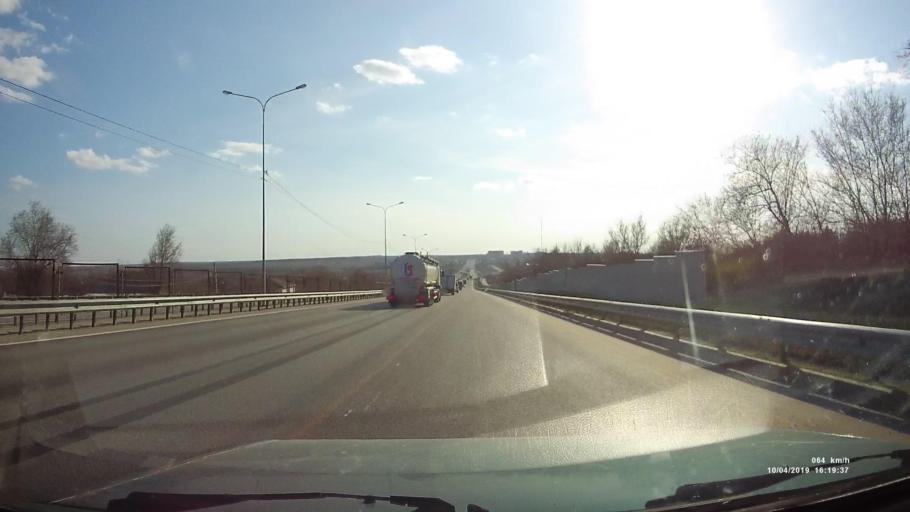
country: RU
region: Rostov
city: Staraya Stanitsa
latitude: 48.3129
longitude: 40.3222
